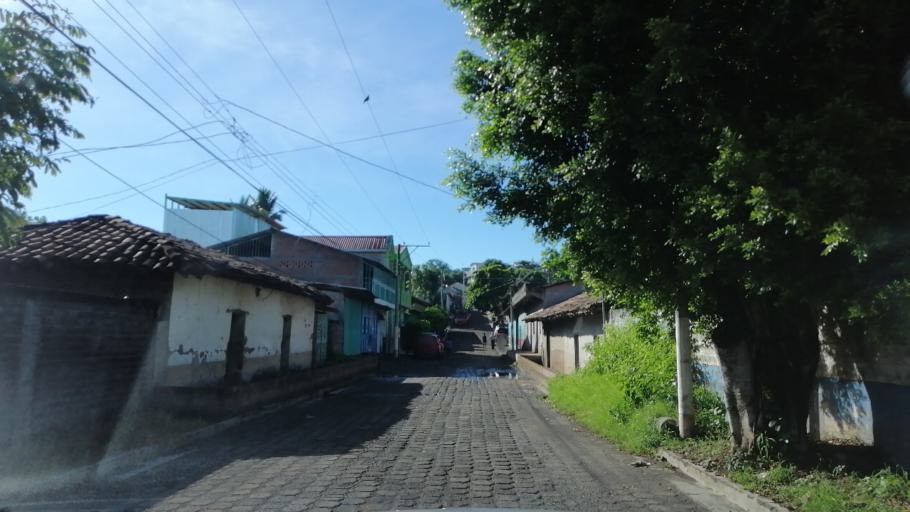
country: SV
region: Morazan
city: Cacaopera
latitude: 13.7750
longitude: -88.0818
